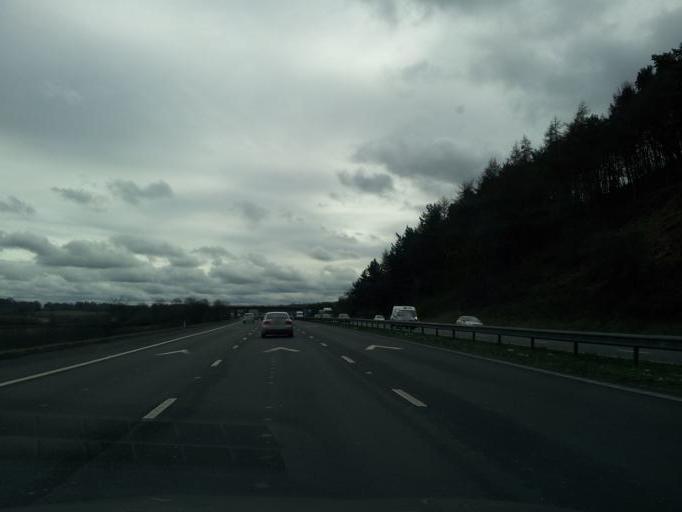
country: GB
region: England
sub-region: Staffordshire
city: Barlaston
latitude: 52.9385
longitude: -2.2152
